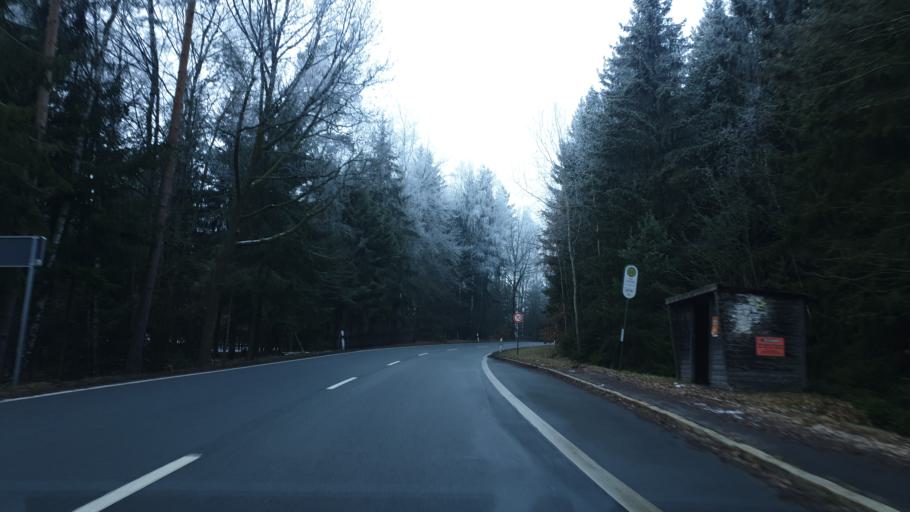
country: DE
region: Saxony
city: Bad Brambach
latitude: 50.2074
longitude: 12.3122
